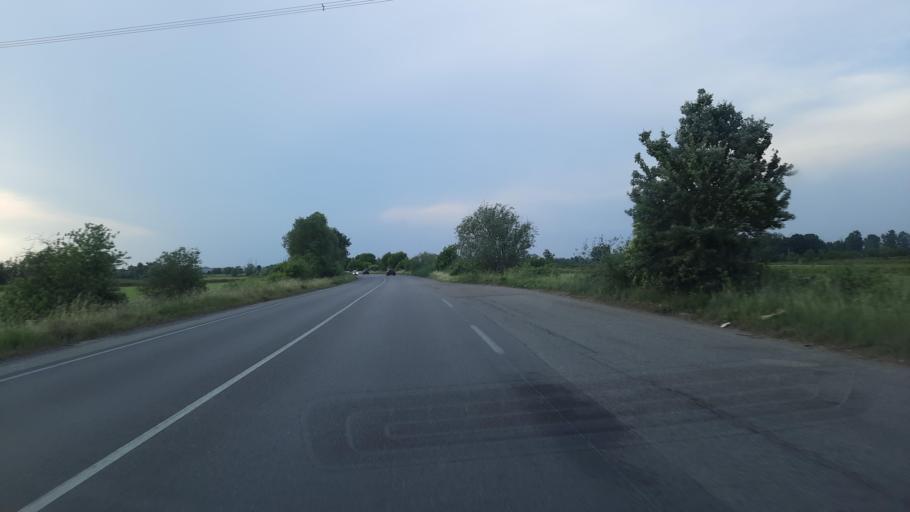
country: IT
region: Lombardy
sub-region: Provincia di Pavia
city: Gropello Cairoli
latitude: 45.1833
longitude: 8.9630
